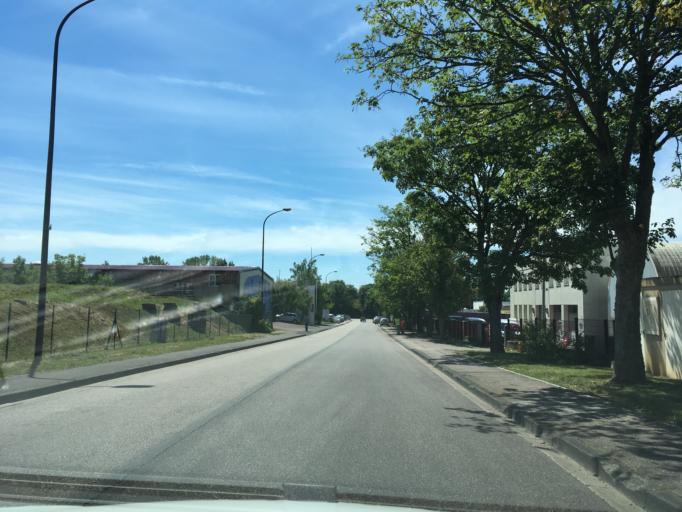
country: FR
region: Lorraine
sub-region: Departement de la Moselle
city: Saint-Julien-les-Metz
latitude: 49.1169
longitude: 6.2364
